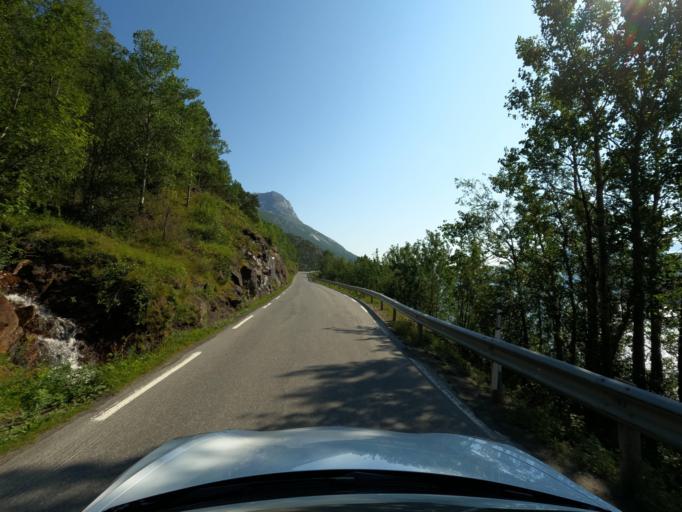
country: NO
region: Nordland
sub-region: Narvik
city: Narvik
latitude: 68.3684
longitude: 17.2525
